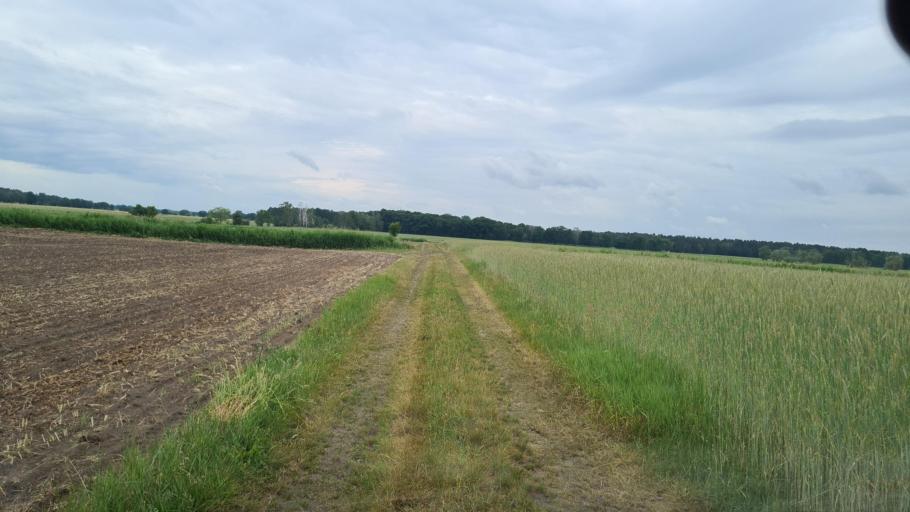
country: DE
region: Brandenburg
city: Bronkow
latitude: 51.6231
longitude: 13.9368
